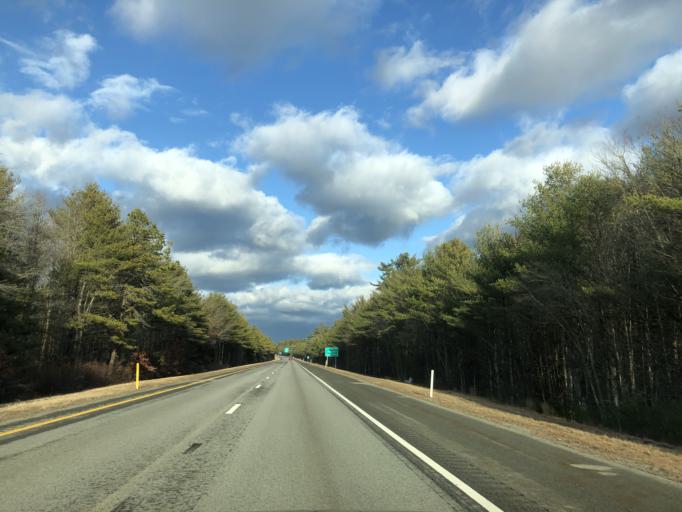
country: US
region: Massachusetts
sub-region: Plymouth County
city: Marion Center
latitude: 41.7123
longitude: -70.7894
